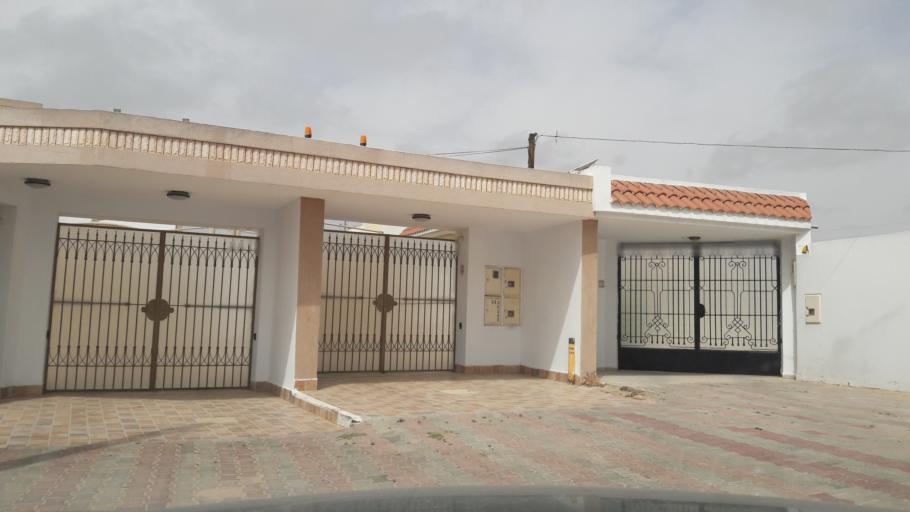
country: TN
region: Safaqis
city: Al Qarmadah
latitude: 34.7910
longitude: 10.7597
